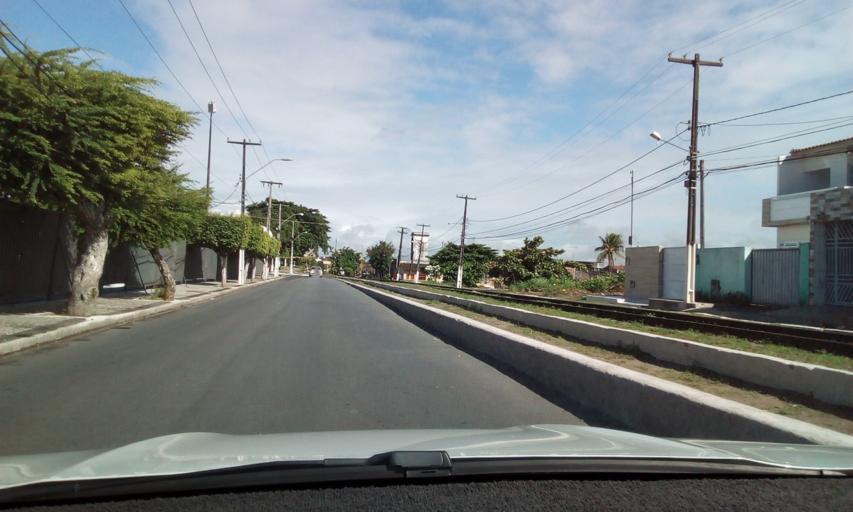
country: BR
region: Paraiba
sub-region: Santa Rita
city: Santa Rita
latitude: -7.1238
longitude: -34.9729
